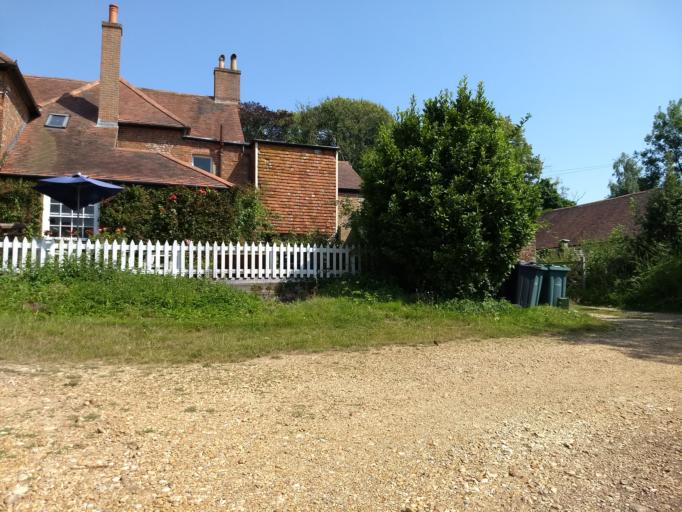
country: GB
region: England
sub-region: Isle of Wight
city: Northwood
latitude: 50.7335
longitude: -1.3122
